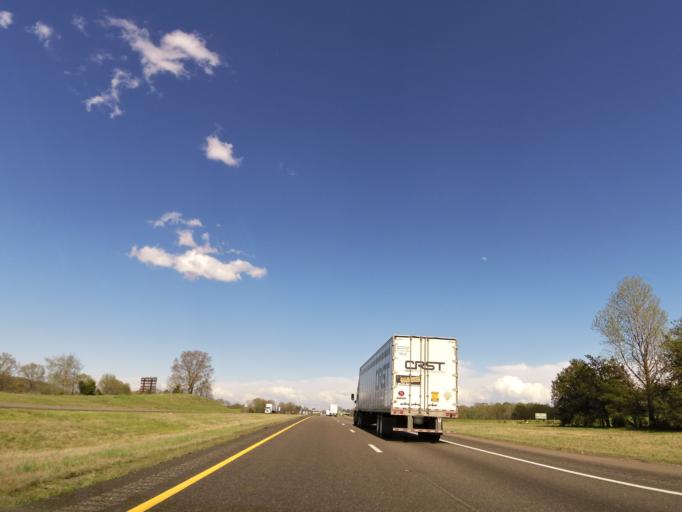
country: US
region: Tennessee
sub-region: Henderson County
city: Lexington
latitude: 35.7854
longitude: -88.4044
